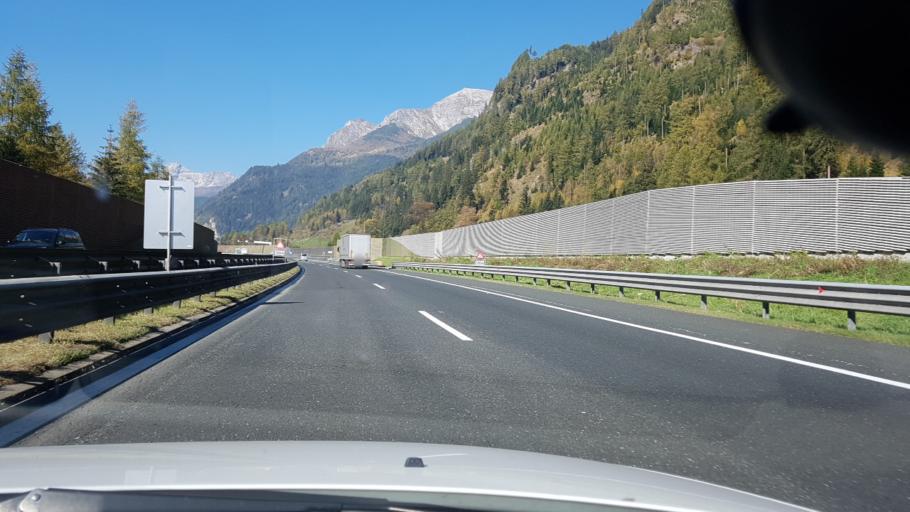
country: AT
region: Salzburg
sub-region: Politischer Bezirk Tamsweg
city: Zederhaus
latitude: 47.1447
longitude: 13.5217
